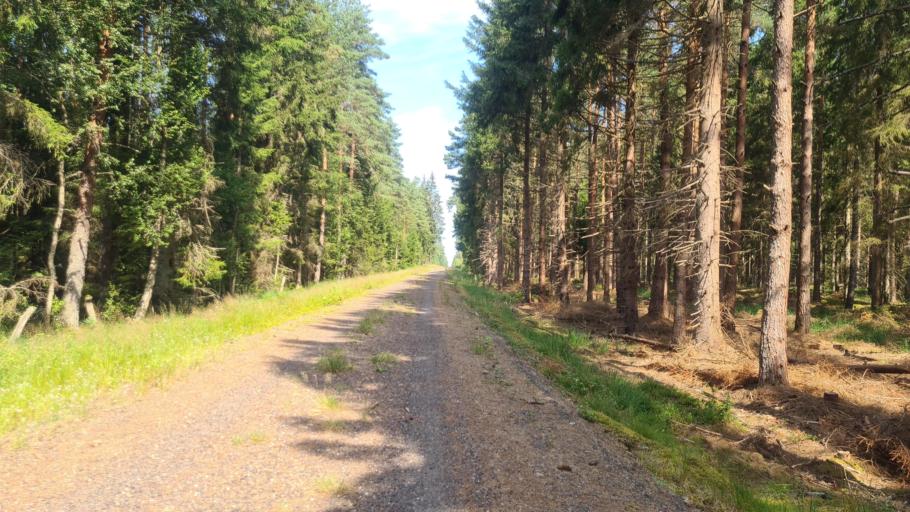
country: SE
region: Kronoberg
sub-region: Ljungby Kommun
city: Lagan
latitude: 56.9575
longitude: 13.9568
